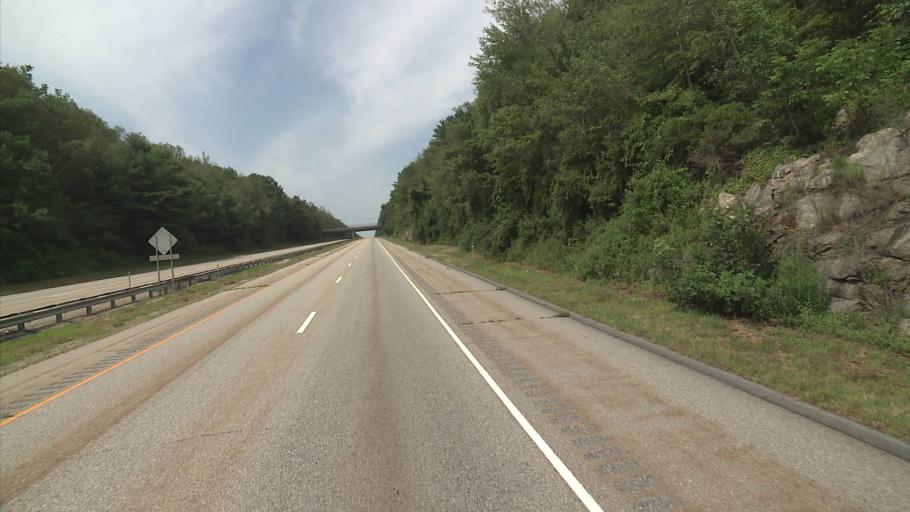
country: US
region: Connecticut
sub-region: Windham County
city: Danielson
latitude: 41.7873
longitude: -71.8088
